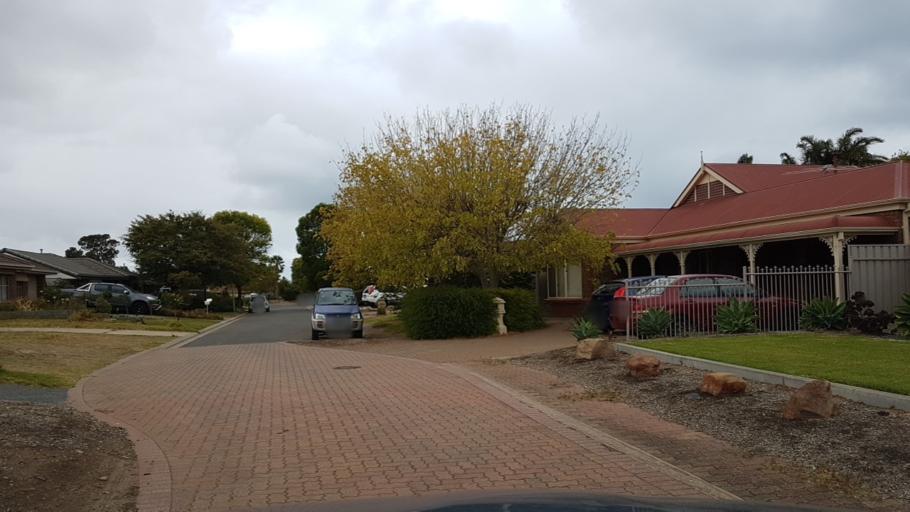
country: AU
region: South Australia
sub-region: Onkaparinga
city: Moana
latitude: -35.1964
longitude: 138.4800
